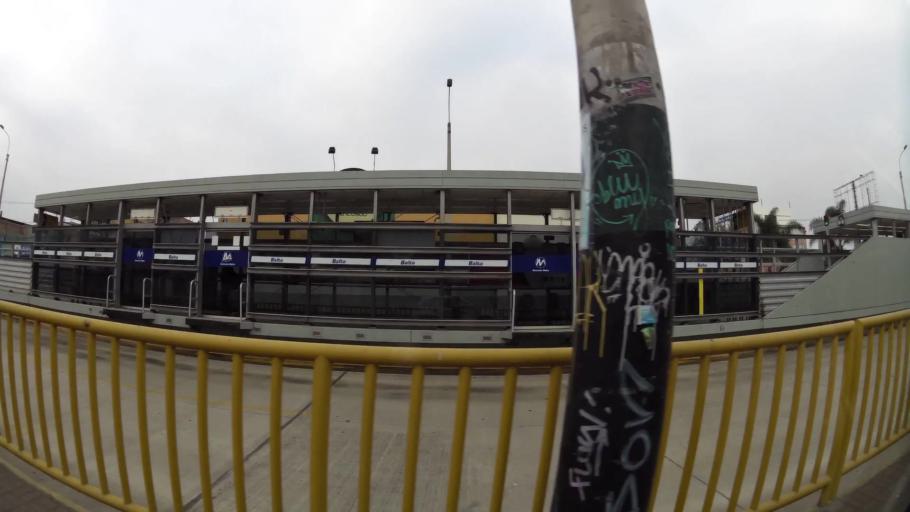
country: PE
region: Lima
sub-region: Lima
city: Surco
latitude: -12.1412
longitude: -77.0178
